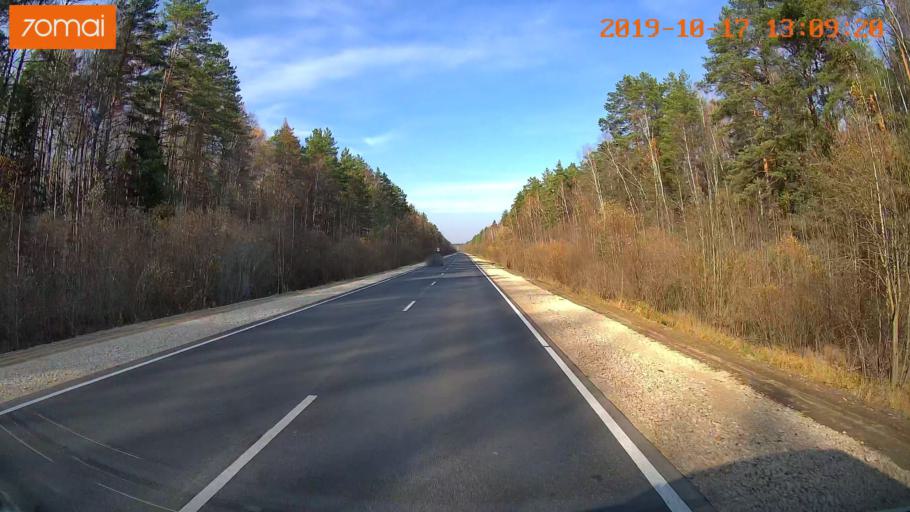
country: RU
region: Rjazan
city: Syntul
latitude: 55.0023
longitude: 41.2637
